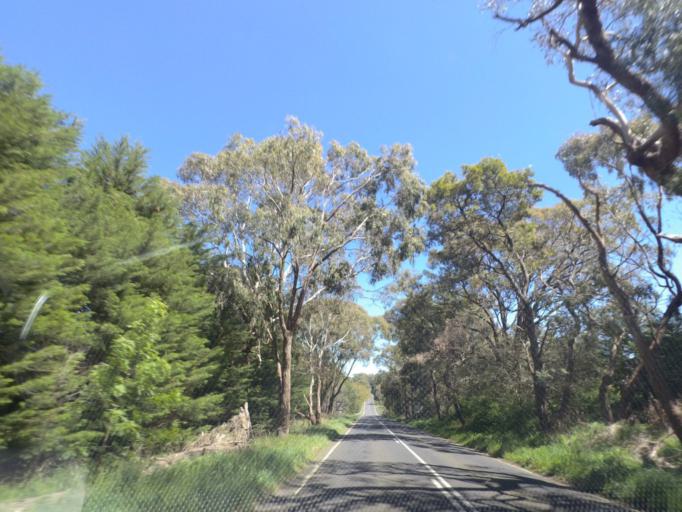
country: AU
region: Victoria
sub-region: Hume
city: Sunbury
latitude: -37.3139
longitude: 144.6713
